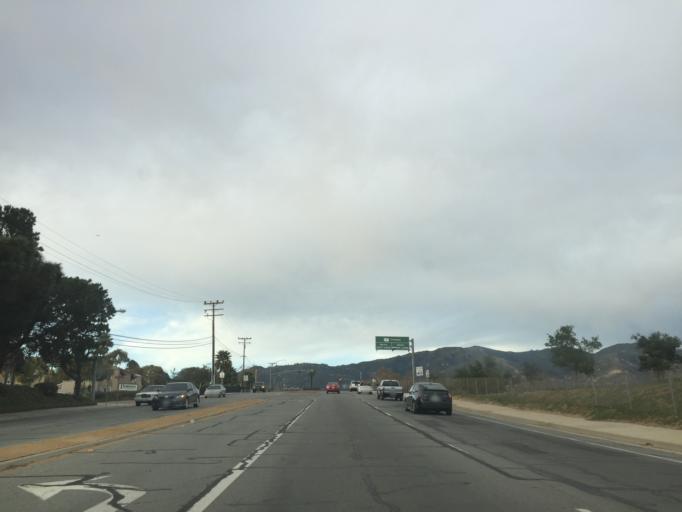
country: US
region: California
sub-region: Santa Barbara County
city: Goleta
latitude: 34.4398
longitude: -119.7893
